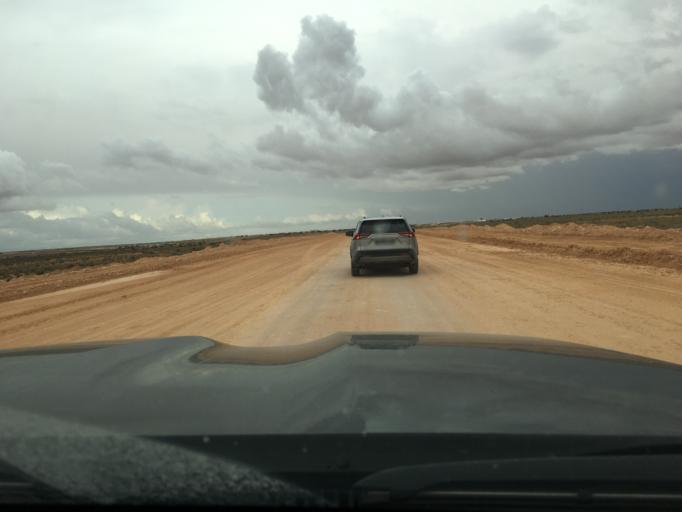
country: TN
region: Madanin
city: Medenine
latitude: 33.2823
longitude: 10.5961
